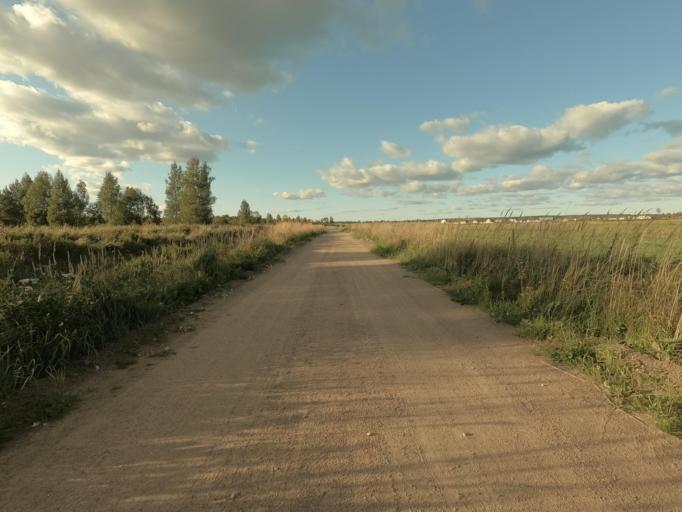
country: RU
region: Leningrad
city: Imeni Sverdlova
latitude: 59.8626
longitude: 30.7306
